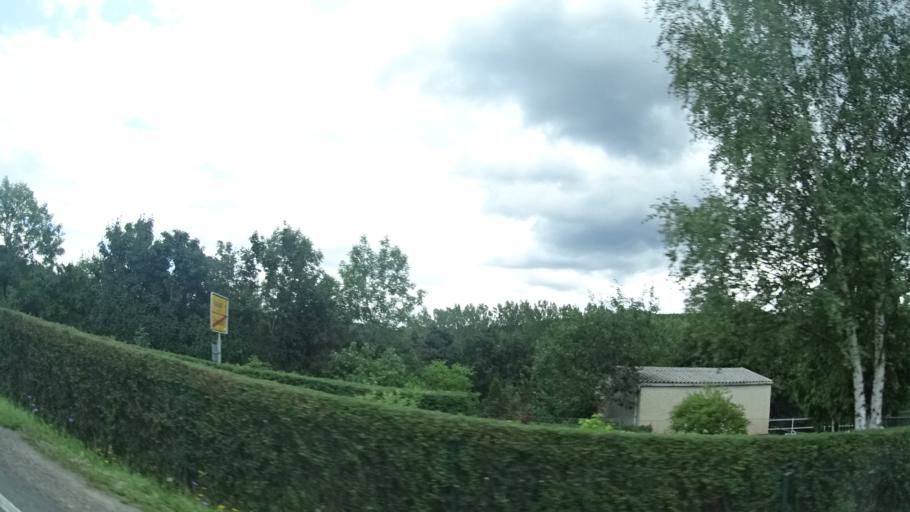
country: DE
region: Thuringia
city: Kaulsdorf
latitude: 50.6219
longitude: 11.4048
